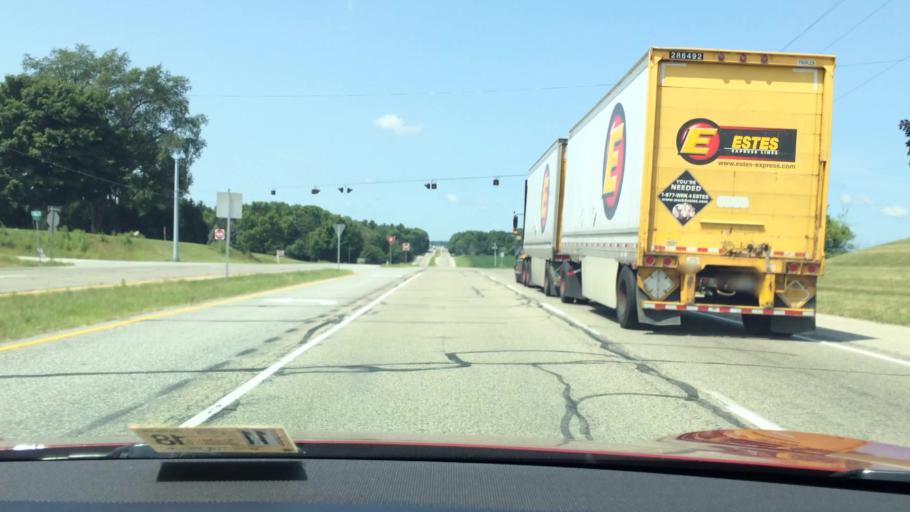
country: US
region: Indiana
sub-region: LaPorte County
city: Hudson Lake
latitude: 41.6727
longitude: -86.5643
